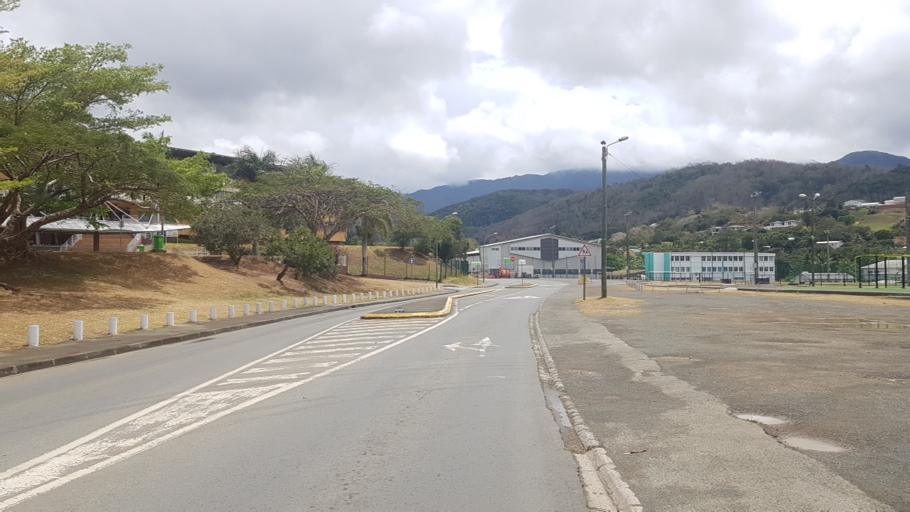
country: NC
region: South Province
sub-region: Dumbea
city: Dumbea
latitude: -22.2080
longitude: 166.4749
